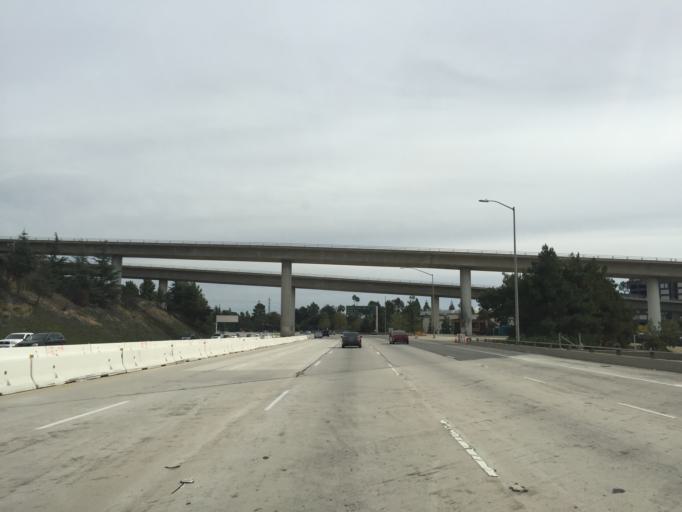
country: US
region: California
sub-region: Los Angeles County
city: La Crescenta-Montrose
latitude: 34.2080
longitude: -118.2192
